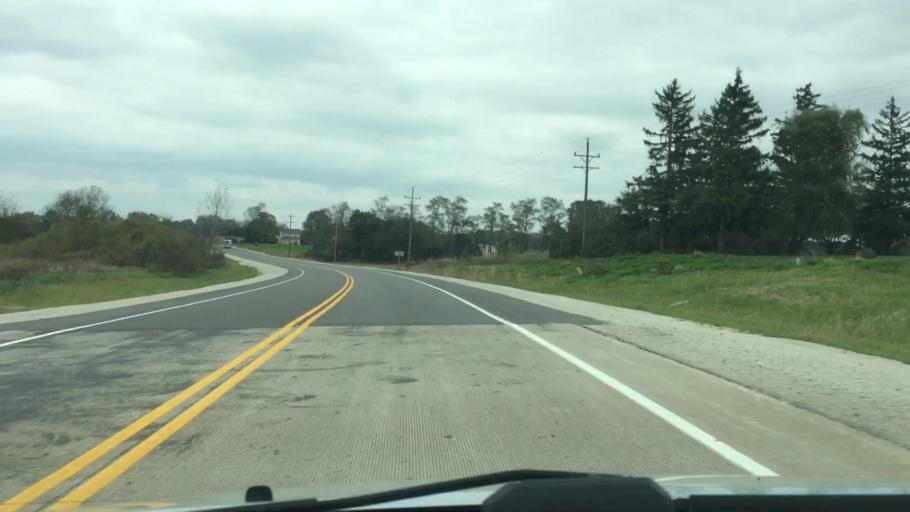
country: US
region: Wisconsin
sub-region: Walworth County
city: Whitewater
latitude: 42.8480
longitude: -88.7823
